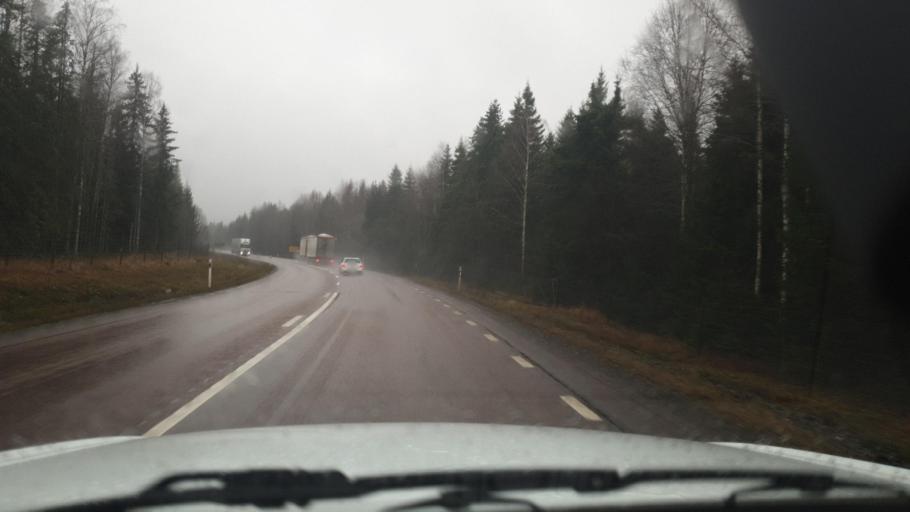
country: SE
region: Vaermland
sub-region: Sunne Kommun
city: Sunne
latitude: 59.7631
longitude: 13.1119
